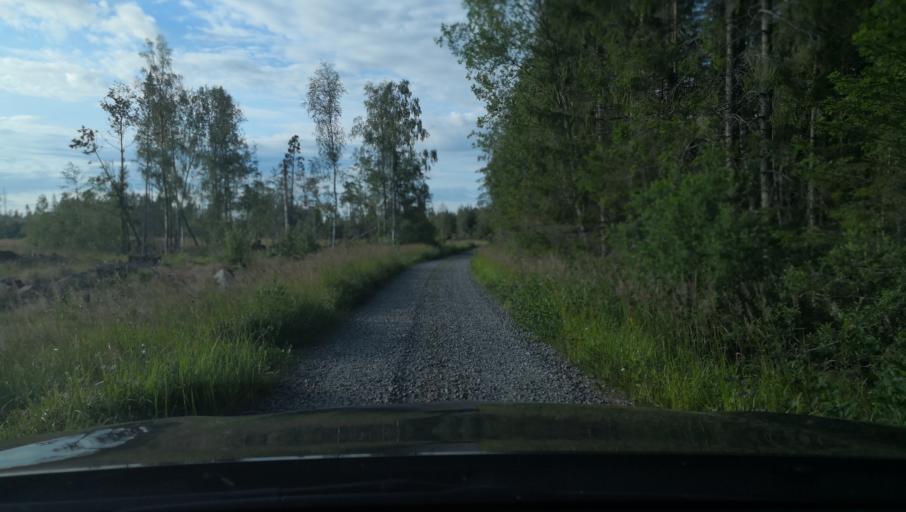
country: SE
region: Uppsala
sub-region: Osthammars Kommun
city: Osterbybruk
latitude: 60.0344
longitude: 17.9194
